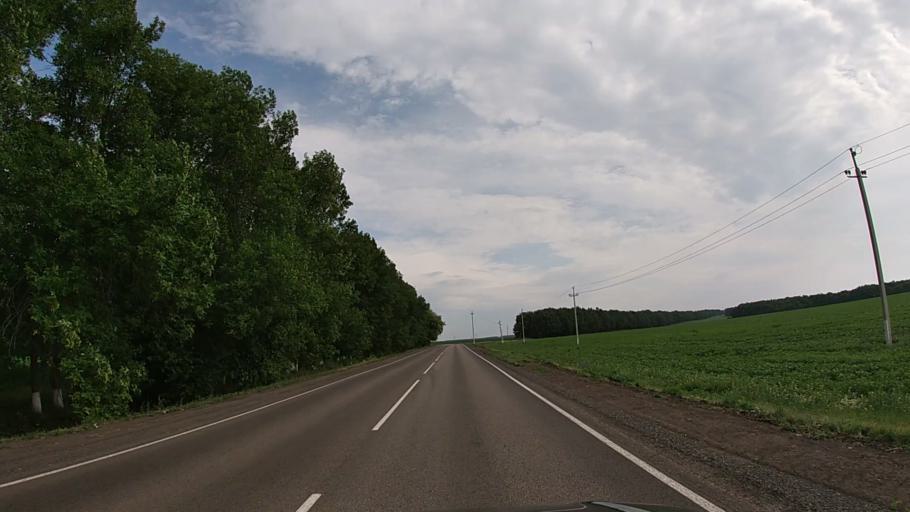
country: RU
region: Belgorod
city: Krasnaya Yaruga
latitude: 50.8122
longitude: 35.5010
